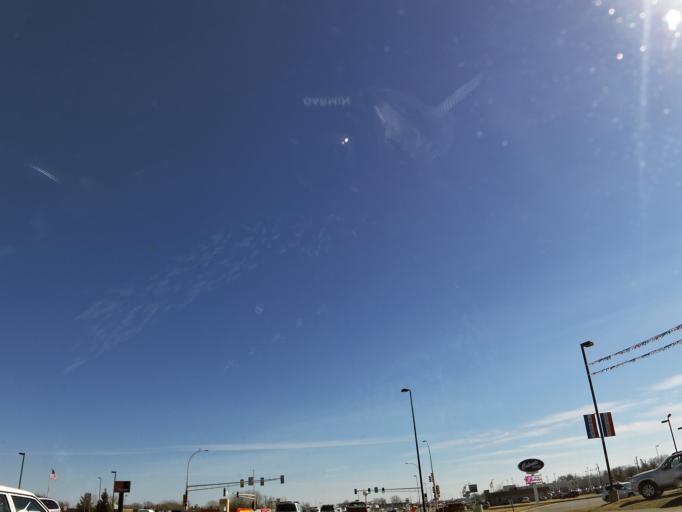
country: US
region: Minnesota
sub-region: Wright County
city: Buffalo
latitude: 45.1774
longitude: -93.8672
